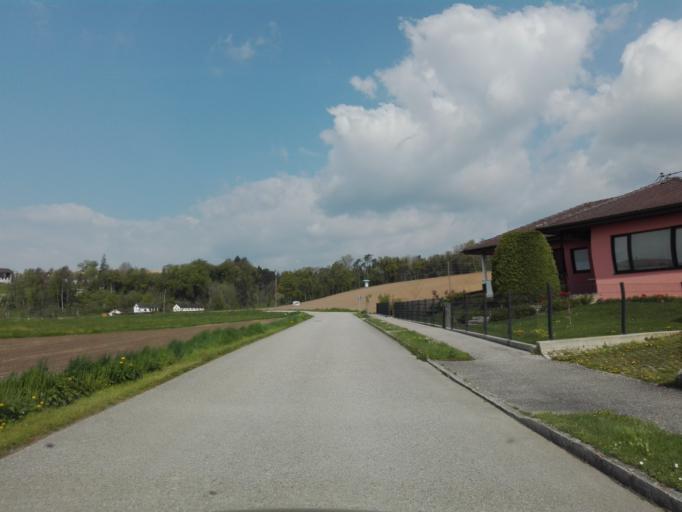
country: AT
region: Upper Austria
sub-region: Politischer Bezirk Perg
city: Perg
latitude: 48.2310
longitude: 14.6922
